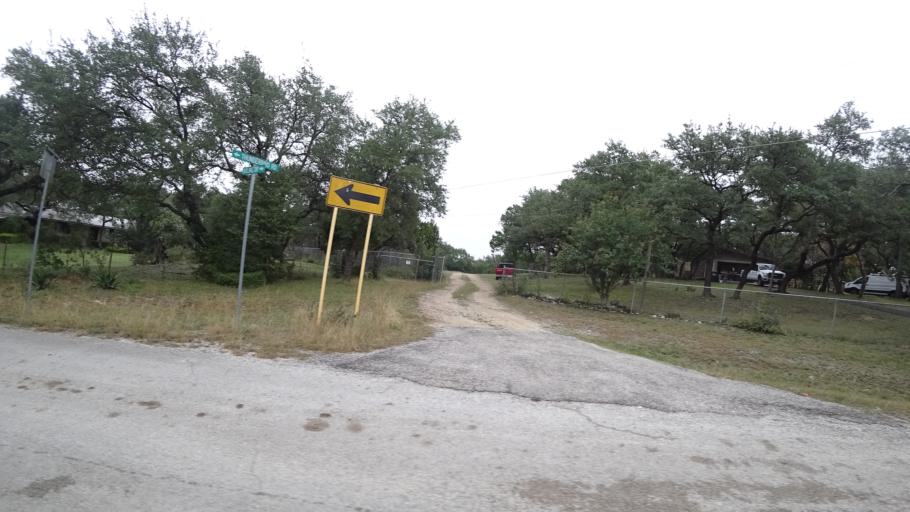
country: US
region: Texas
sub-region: Travis County
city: Barton Creek
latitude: 30.2332
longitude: -97.8976
